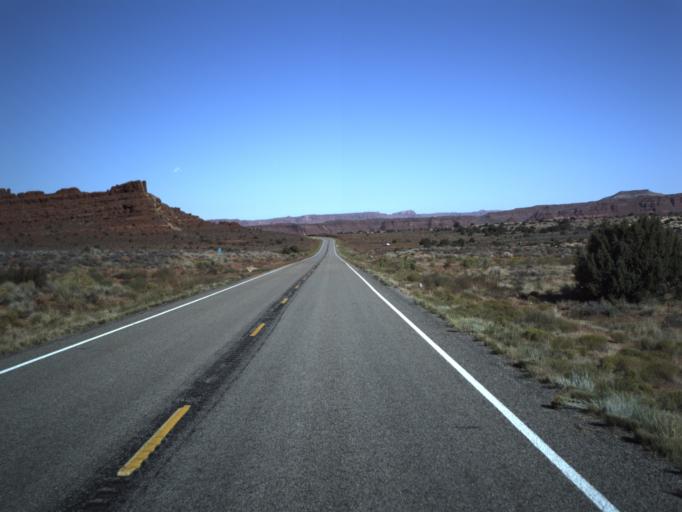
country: US
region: Utah
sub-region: San Juan County
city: Blanding
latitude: 37.7938
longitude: -110.3015
